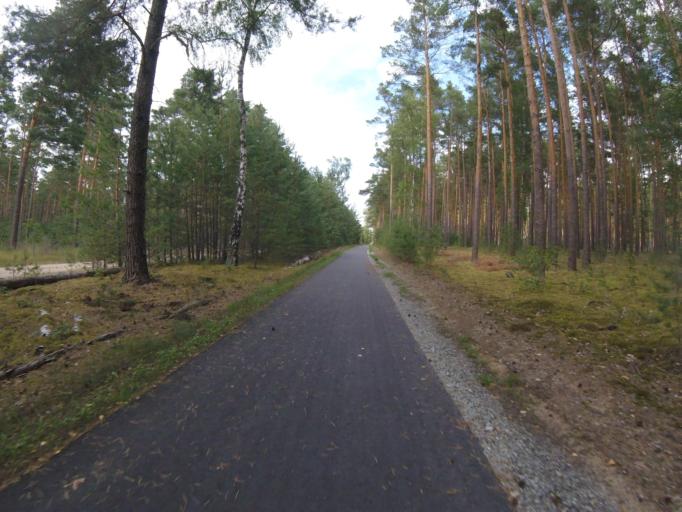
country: DE
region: Brandenburg
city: Halbe
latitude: 52.1551
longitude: 13.7472
